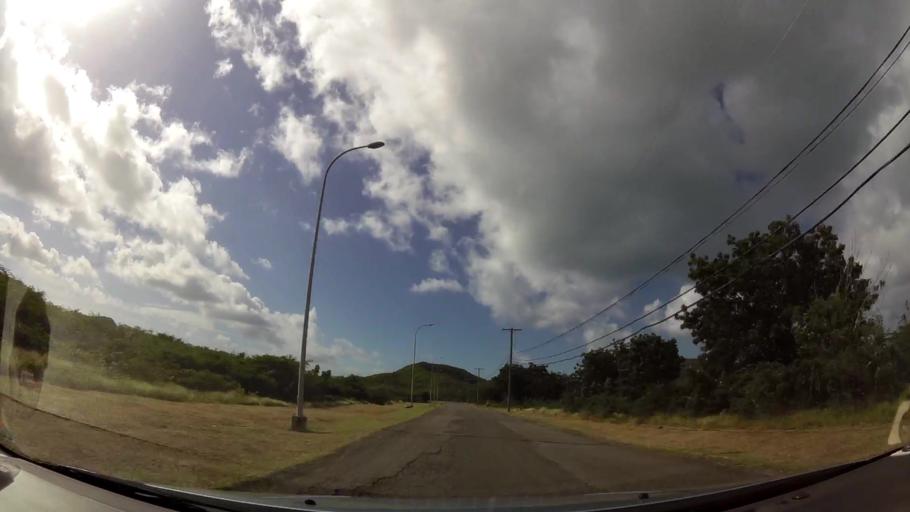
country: AG
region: Saint John
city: Saint John's
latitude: 17.1176
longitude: -61.8653
